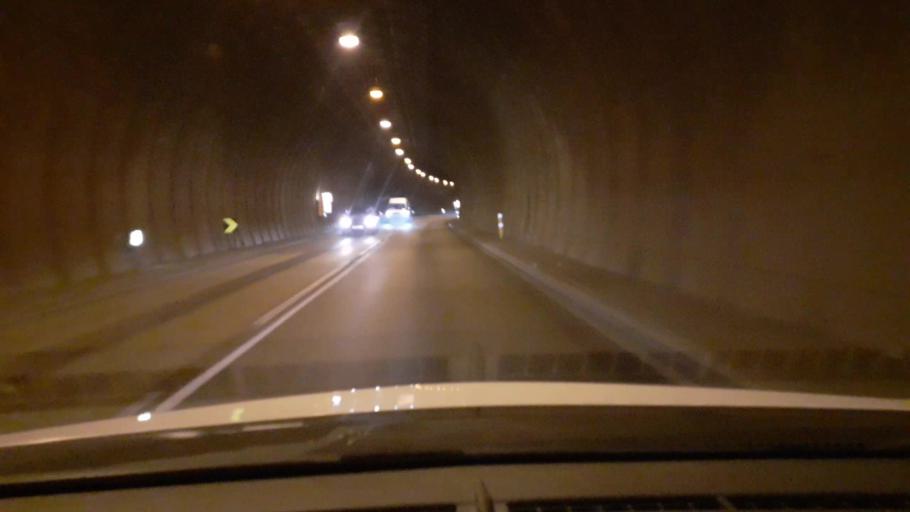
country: IS
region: Capital Region
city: Reykjavik
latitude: 64.2865
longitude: -21.8496
